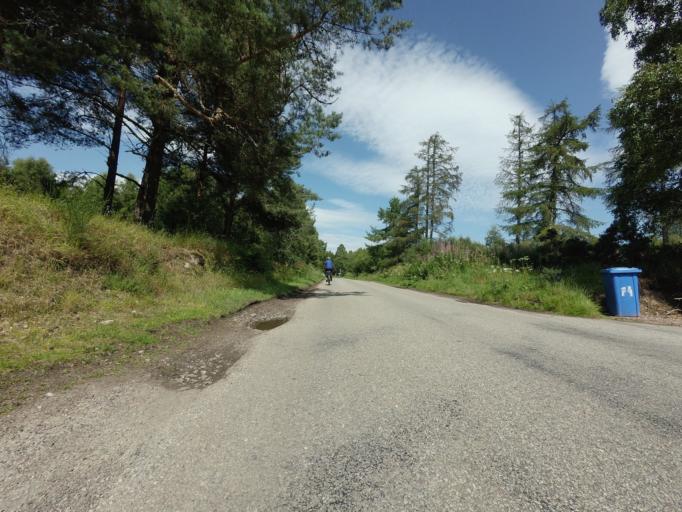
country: GB
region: Scotland
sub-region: Highland
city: Inverness
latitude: 57.5325
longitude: -4.3215
